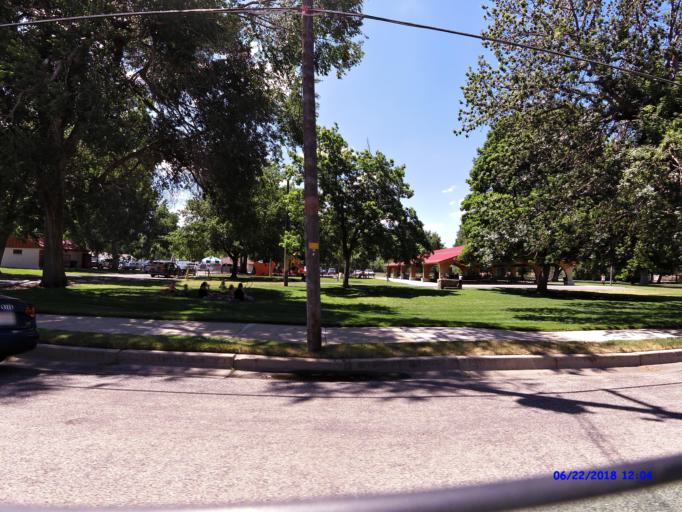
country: US
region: Utah
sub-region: Weber County
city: Ogden
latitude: 41.2378
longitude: -111.9593
